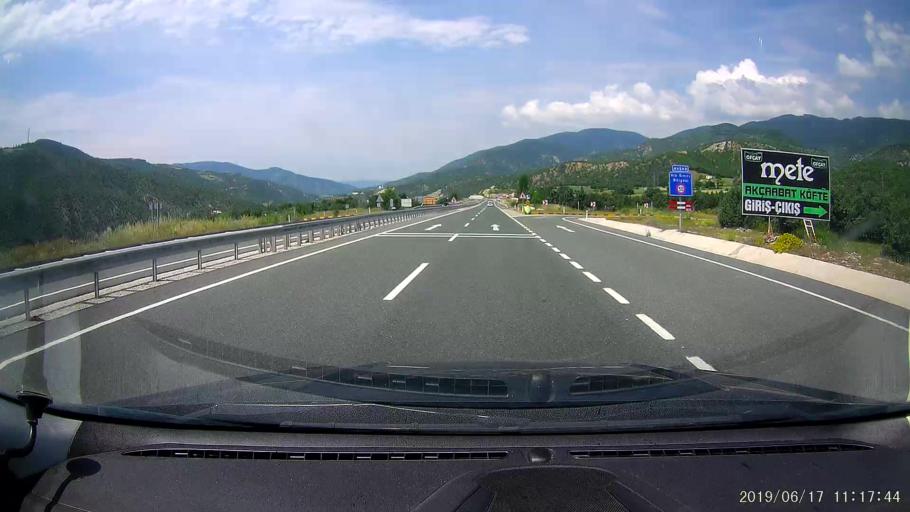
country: TR
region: Kastamonu
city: Tosya
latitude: 40.9403
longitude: 33.8680
